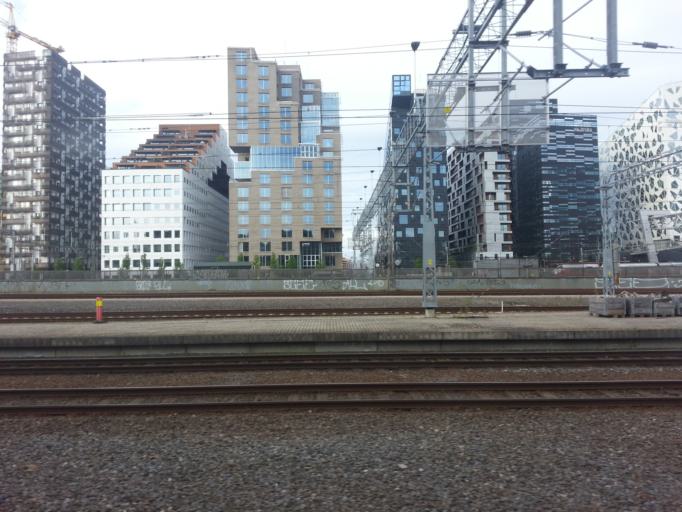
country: NO
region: Oslo
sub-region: Oslo
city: Oslo
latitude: 59.9097
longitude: 10.7616
